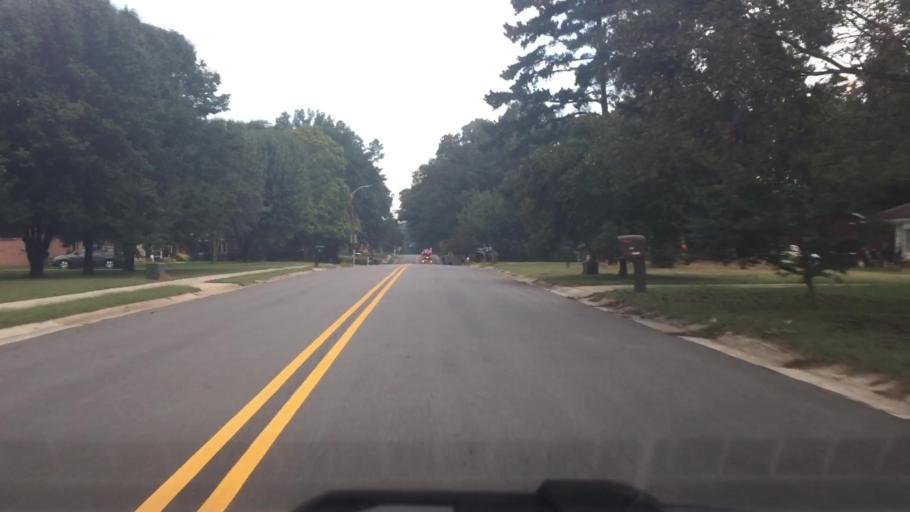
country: US
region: North Carolina
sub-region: Iredell County
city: Mooresville
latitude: 35.5717
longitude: -80.7999
